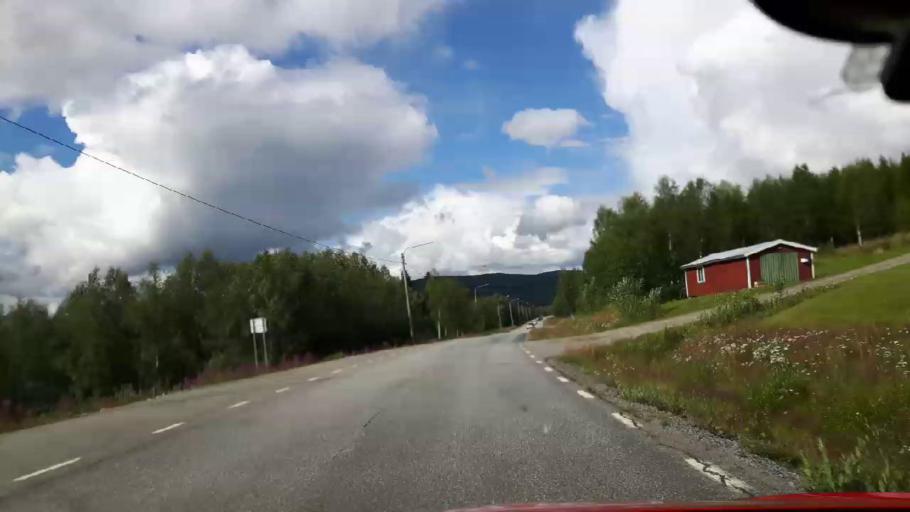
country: NO
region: Nordland
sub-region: Hattfjelldal
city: Hattfjelldal
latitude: 65.0632
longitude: 14.8647
